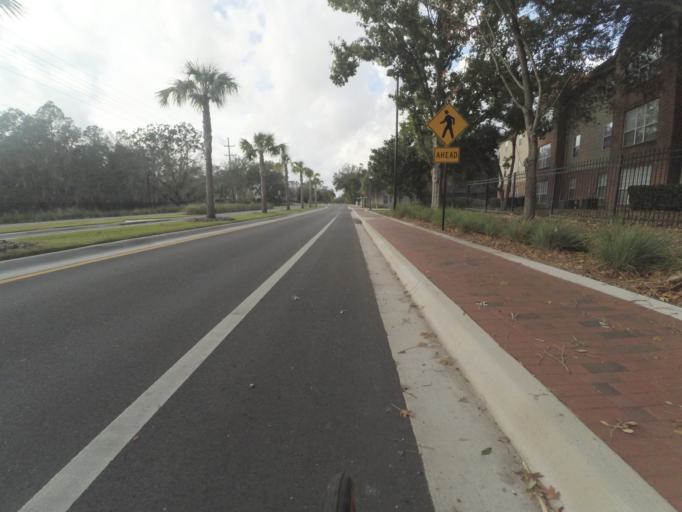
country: US
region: Florida
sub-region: Alachua County
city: Gainesville
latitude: 29.6434
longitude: -82.3323
